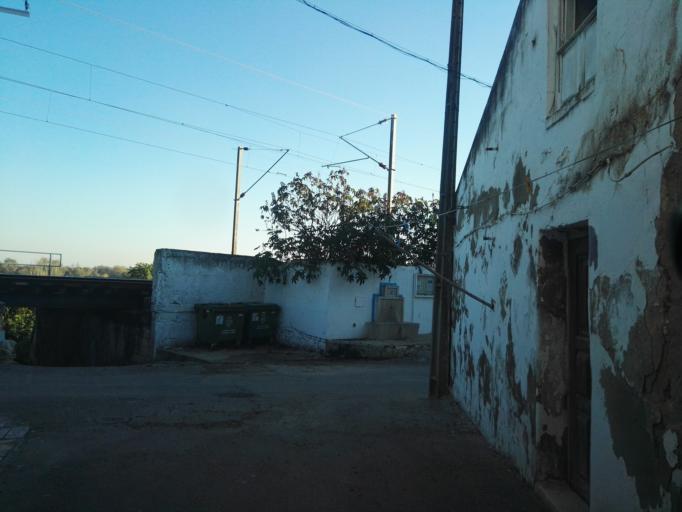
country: PT
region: Santarem
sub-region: Santarem
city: Santarem
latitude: 39.2307
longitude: -8.6747
